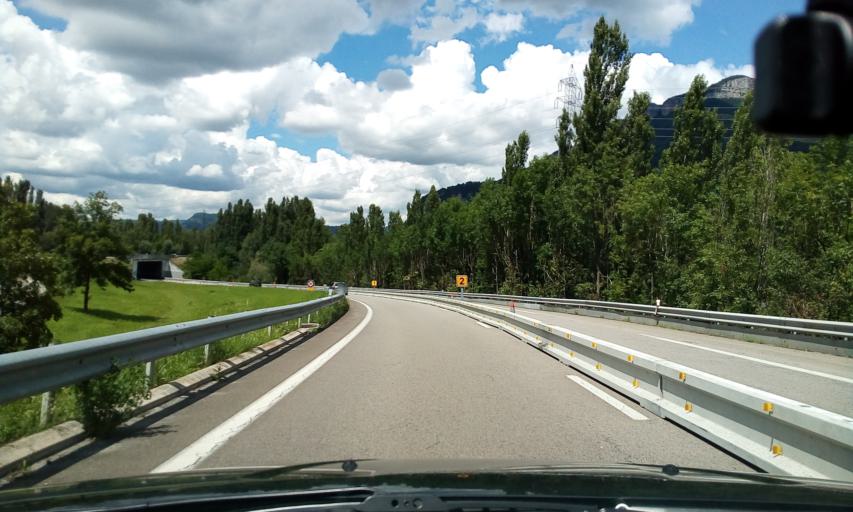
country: FR
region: Rhone-Alpes
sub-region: Departement de l'Isere
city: Voreppe
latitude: 45.2954
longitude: 5.6221
